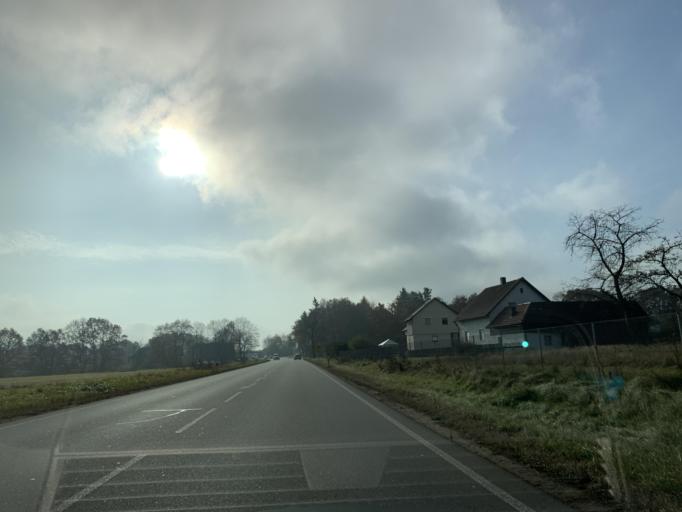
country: DE
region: Bavaria
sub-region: Upper Palatinate
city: Bruck in der Oberpfalz
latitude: 49.2614
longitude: 12.2964
